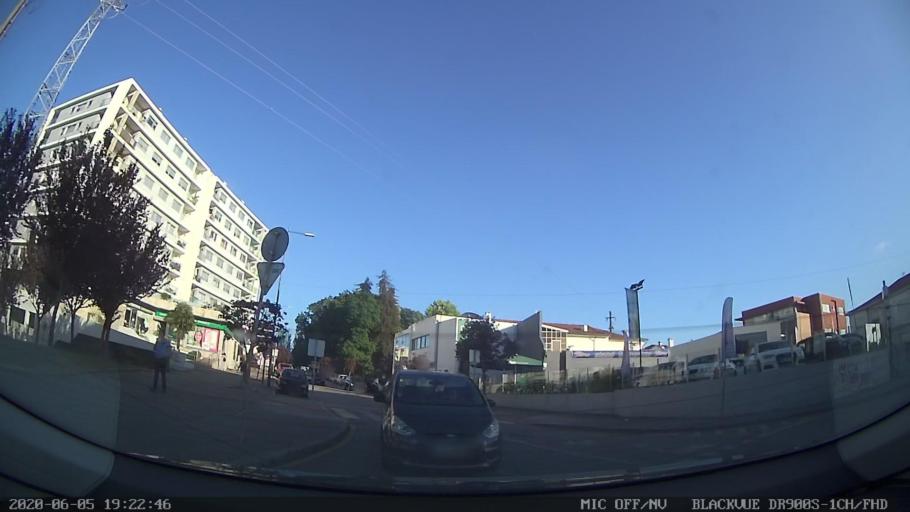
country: PT
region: Porto
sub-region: Valongo
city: Ermesinde
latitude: 41.2132
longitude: -8.5493
